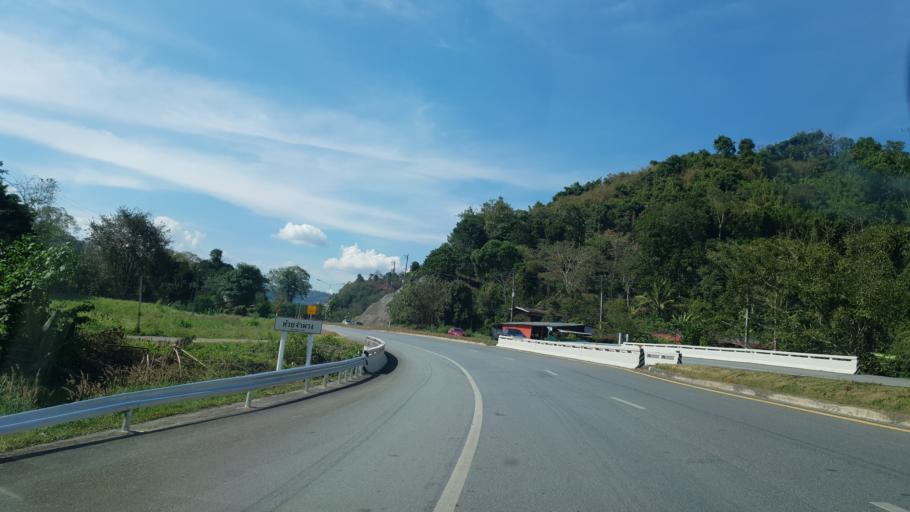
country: TH
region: Phrae
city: Den Chai
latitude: 17.8173
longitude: 100.1010
